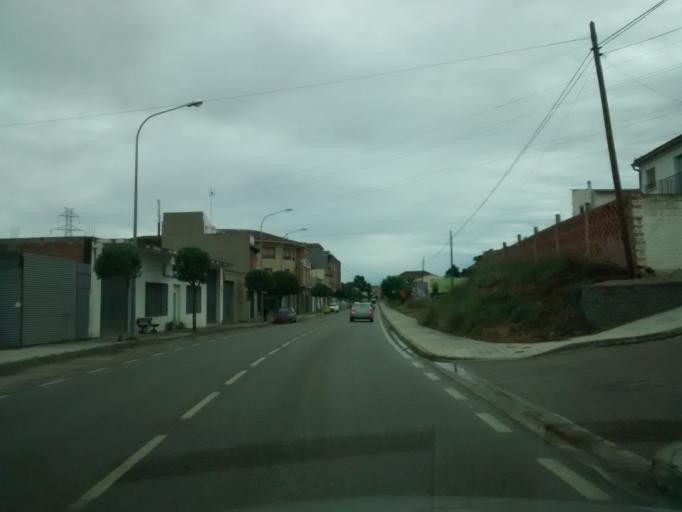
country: ES
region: Aragon
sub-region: Provincia de Zaragoza
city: Caspe
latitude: 41.2271
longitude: -0.0337
